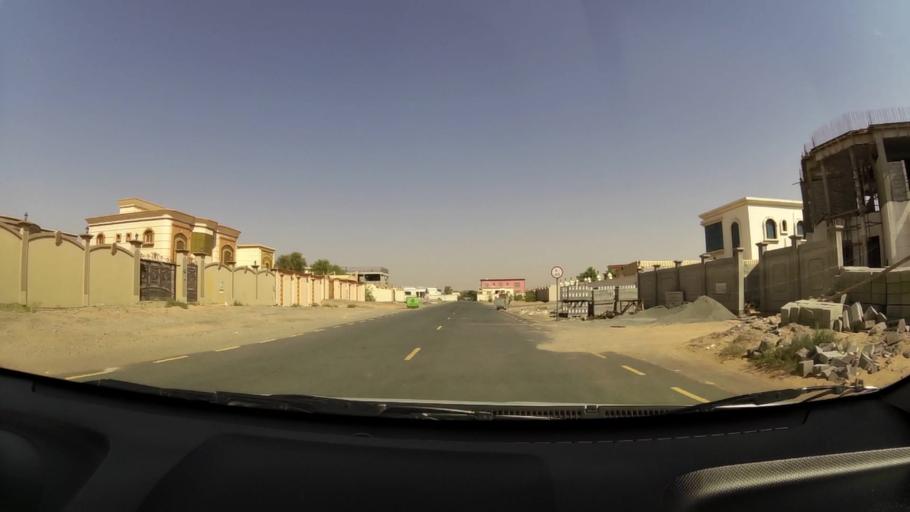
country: AE
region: Umm al Qaywayn
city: Umm al Qaywayn
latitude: 25.4721
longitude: 55.6130
